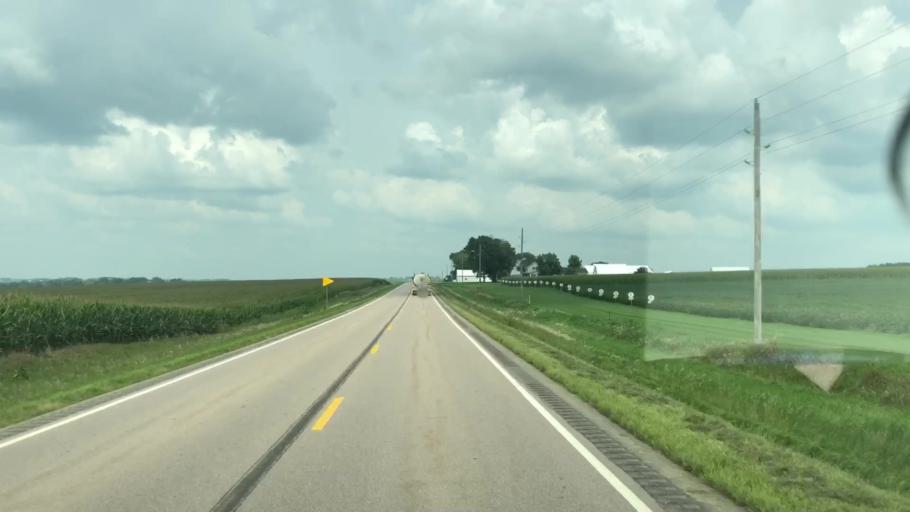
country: US
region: Iowa
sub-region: Plymouth County
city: Remsen
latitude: 42.8009
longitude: -95.9577
